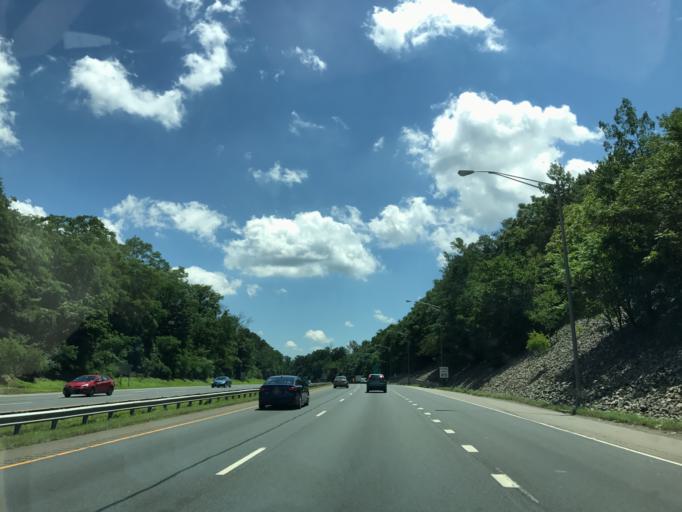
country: US
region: New Jersey
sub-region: Morris County
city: Morristown
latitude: 40.8021
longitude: -74.4429
